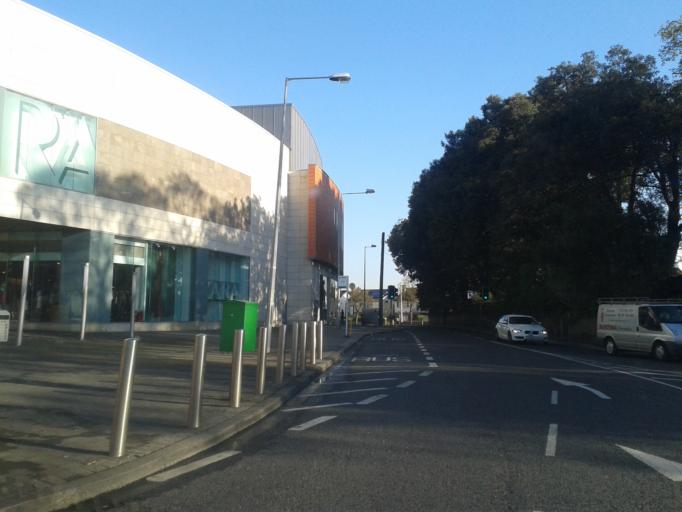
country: IE
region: Leinster
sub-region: Fingal County
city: Swords
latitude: 53.4544
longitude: -6.2184
